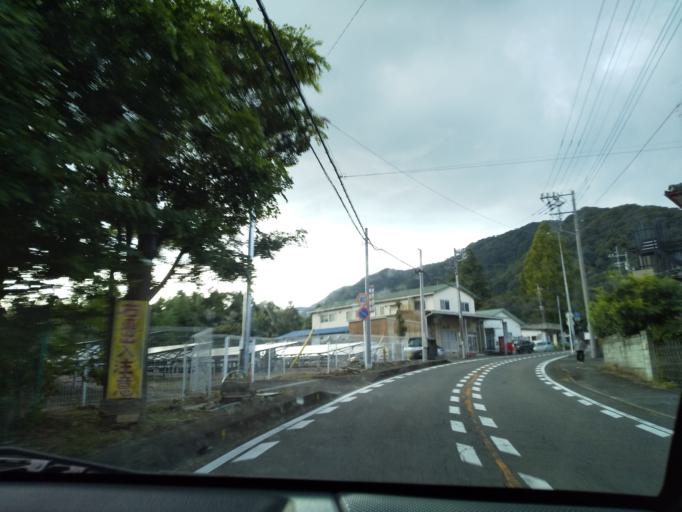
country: JP
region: Tokyo
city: Hachioji
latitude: 35.5910
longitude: 139.2633
